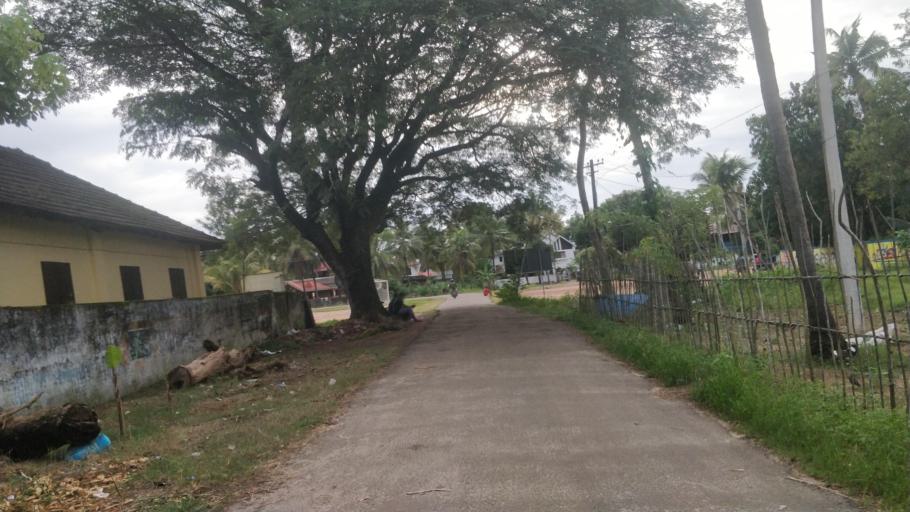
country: IN
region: Kerala
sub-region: Alappuzha
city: Shertallai
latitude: 9.6950
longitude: 76.3621
